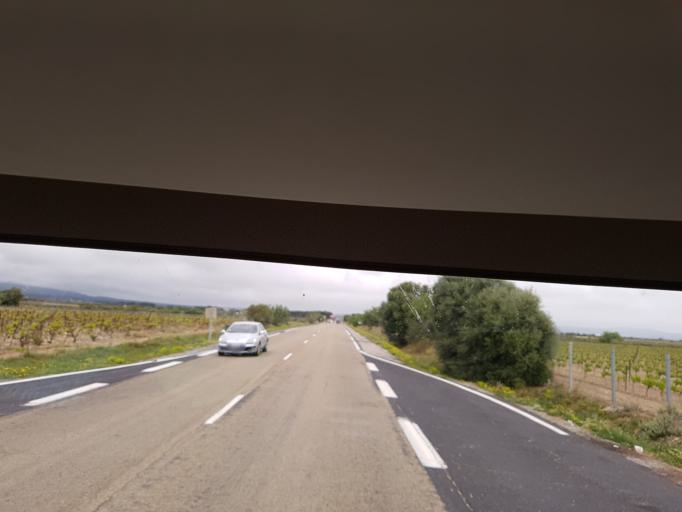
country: FR
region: Languedoc-Roussillon
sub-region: Departement de l'Aude
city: Leucate
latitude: 42.9247
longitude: 2.9947
